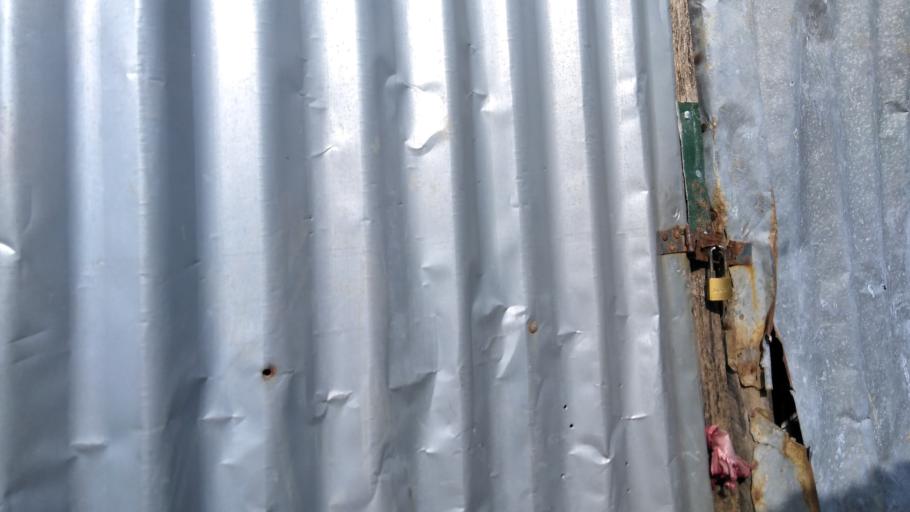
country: NG
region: Ondo
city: Igbekebo
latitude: 5.9268
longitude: 4.9613
